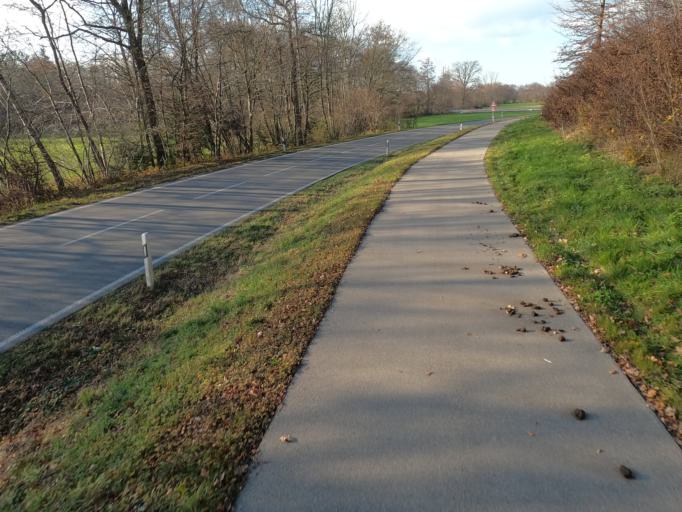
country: DE
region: Baden-Wuerttemberg
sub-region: Regierungsbezirk Stuttgart
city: Schlierbach
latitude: 48.6677
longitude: 9.5321
